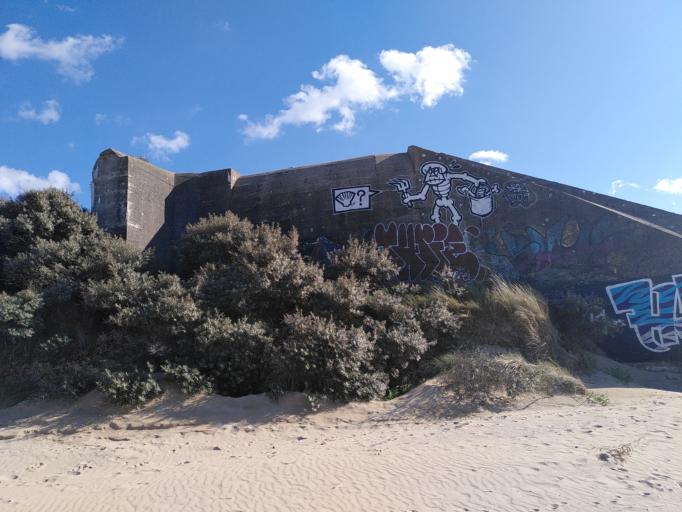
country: FR
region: Nord-Pas-de-Calais
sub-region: Departement du Pas-de-Calais
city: Marck
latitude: 50.9918
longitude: 1.9821
